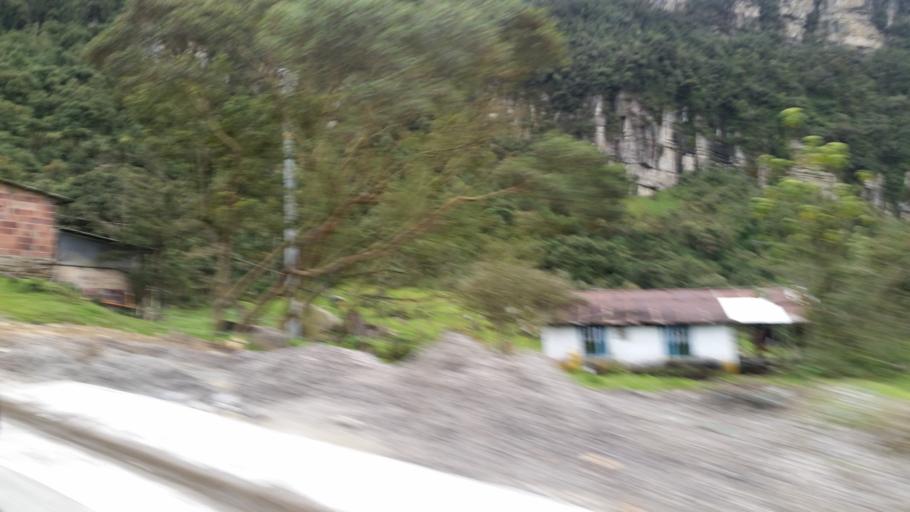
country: CO
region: Cundinamarca
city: Choachi
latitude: 4.5650
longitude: -73.9732
